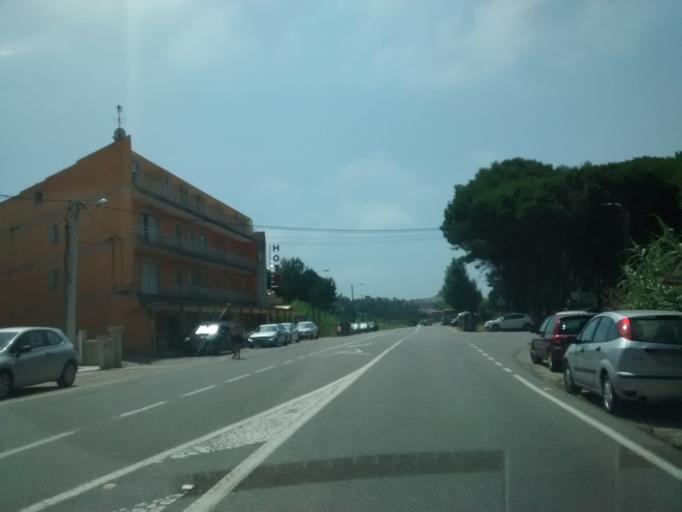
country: ES
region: Galicia
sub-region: Provincia de Pontevedra
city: Sanxenxo
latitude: 42.3980
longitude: -8.8452
